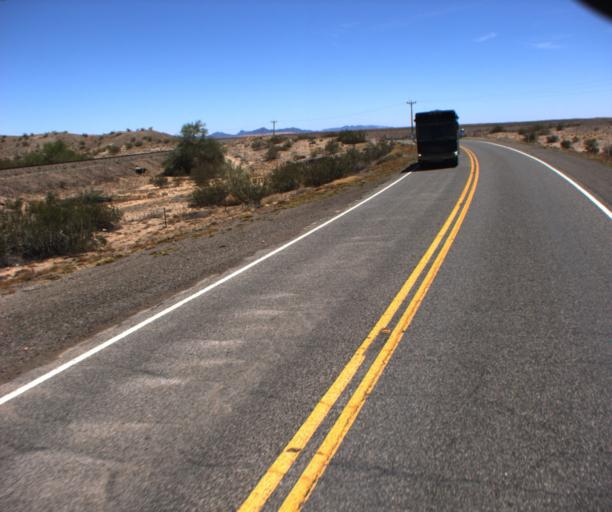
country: US
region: Arizona
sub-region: La Paz County
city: Parker
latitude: 34.0101
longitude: -114.2433
